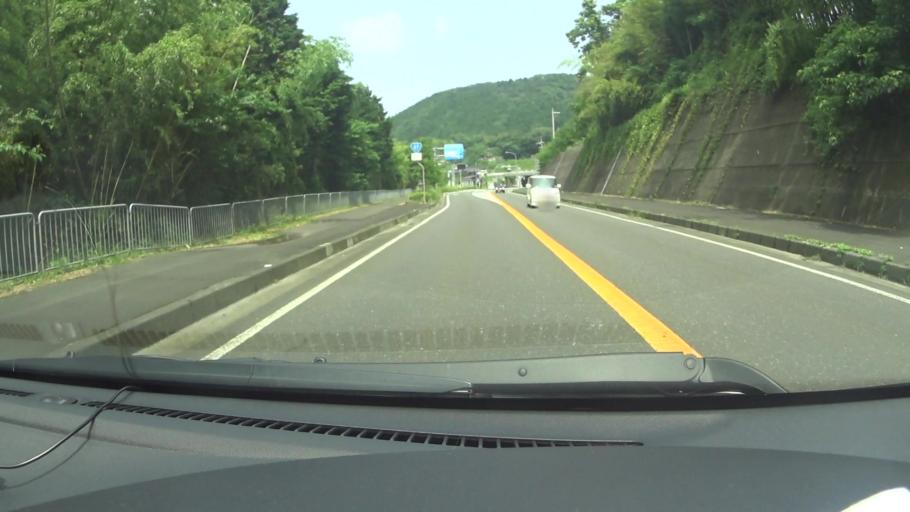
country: JP
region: Kyoto
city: Ayabe
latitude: 35.2602
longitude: 135.4092
